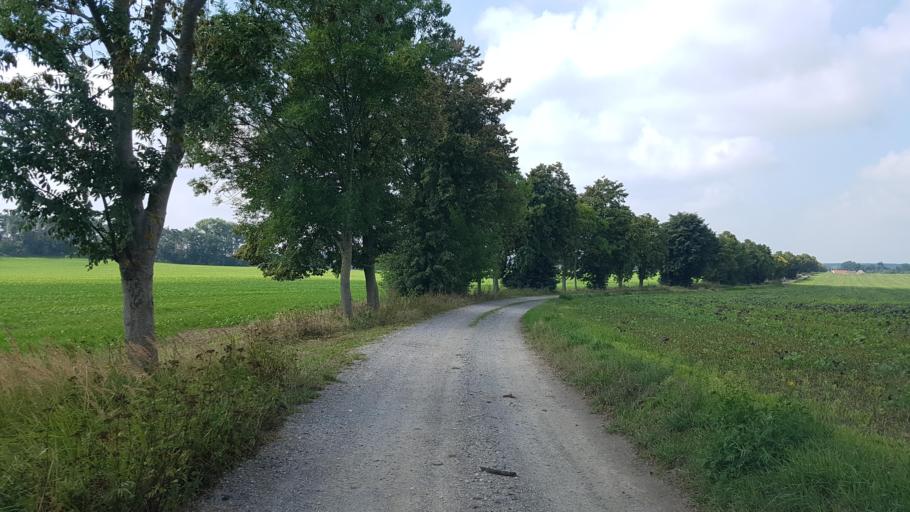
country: DE
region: Brandenburg
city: Luckau
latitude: 51.8154
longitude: 13.6196
